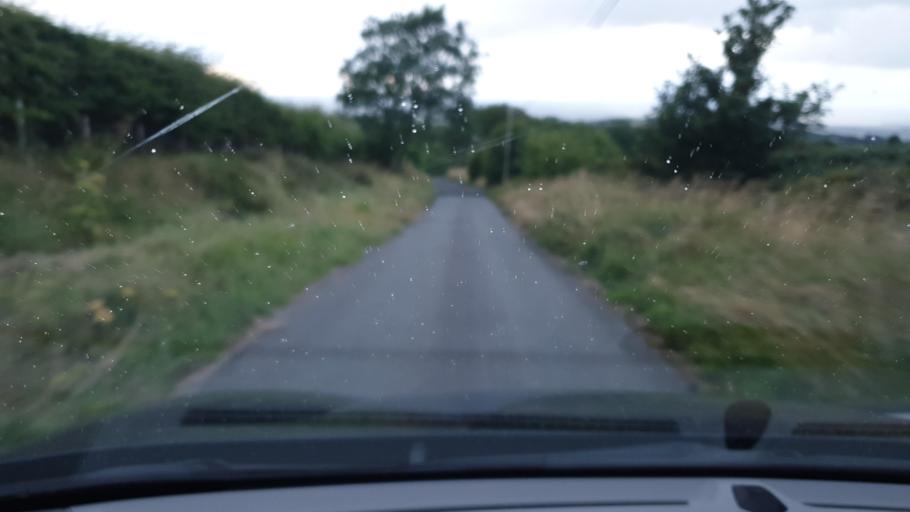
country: IE
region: Leinster
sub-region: Wicklow
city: Blessington
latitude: 53.2244
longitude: -6.5034
